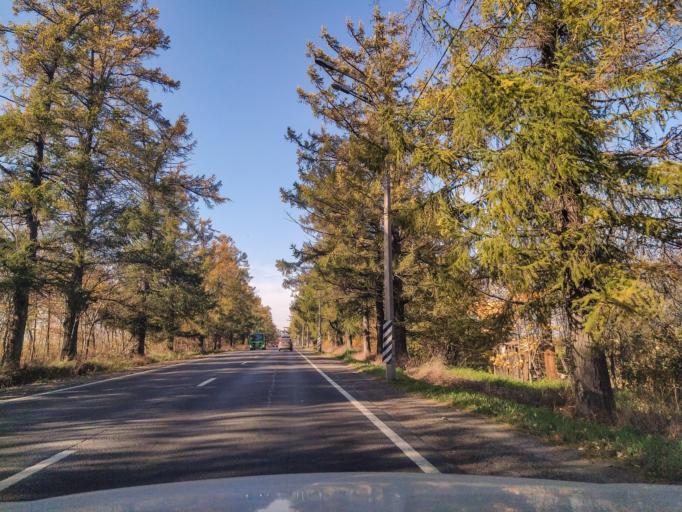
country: RU
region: St.-Petersburg
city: Aleksandrovskaya
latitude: 59.7057
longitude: 30.3398
